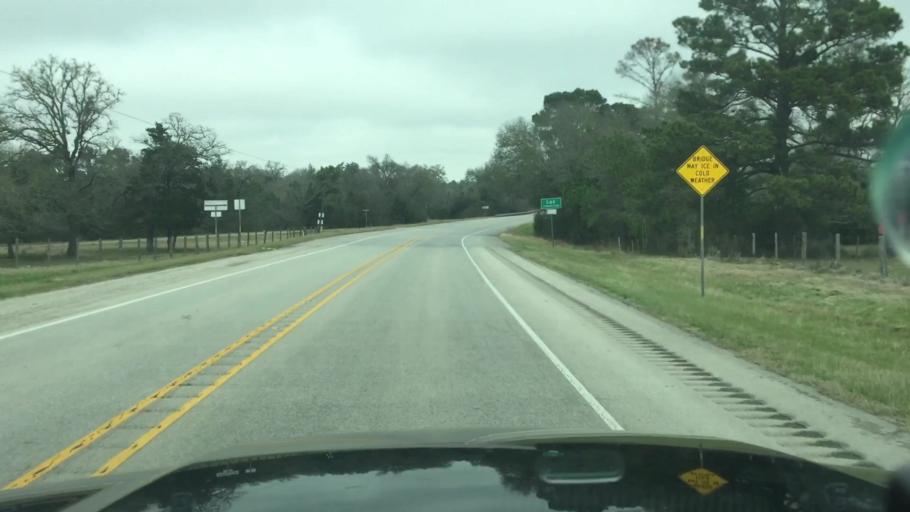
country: US
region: Texas
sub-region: Lee County
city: Giddings
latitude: 30.0816
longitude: -96.9172
